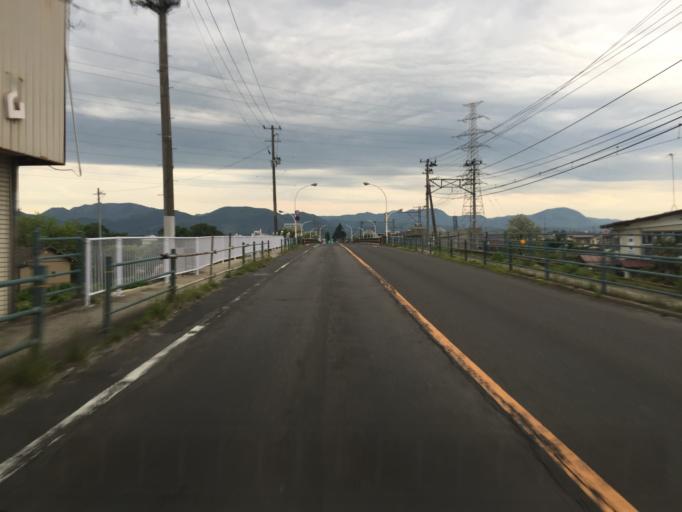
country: JP
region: Fukushima
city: Fukushima-shi
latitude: 37.7805
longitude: 140.4435
